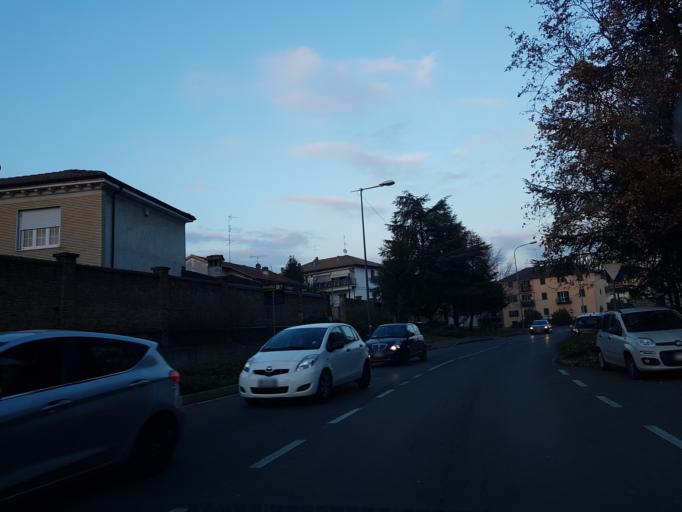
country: IT
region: Piedmont
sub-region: Provincia di Alessandria
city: Novi Ligure
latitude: 44.7650
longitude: 8.7807
